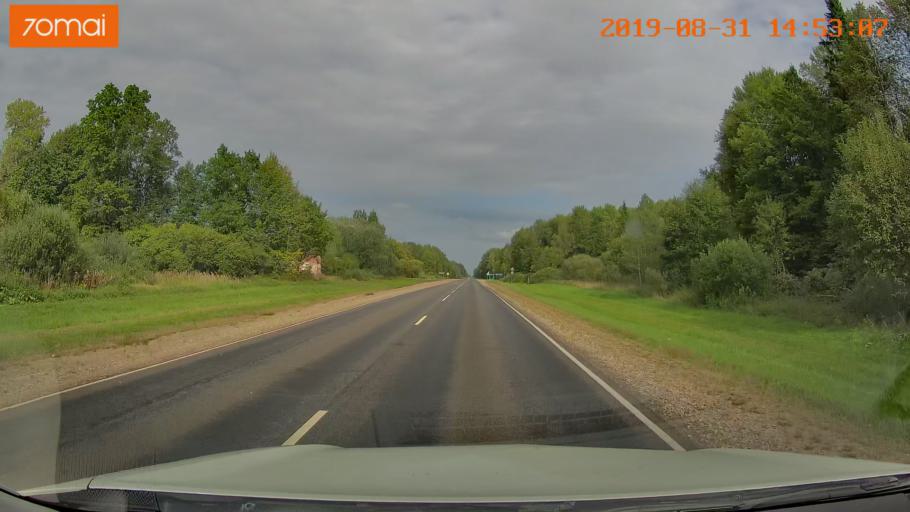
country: RU
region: Kaluga
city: Spas-Demensk
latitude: 54.2809
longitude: 33.8563
